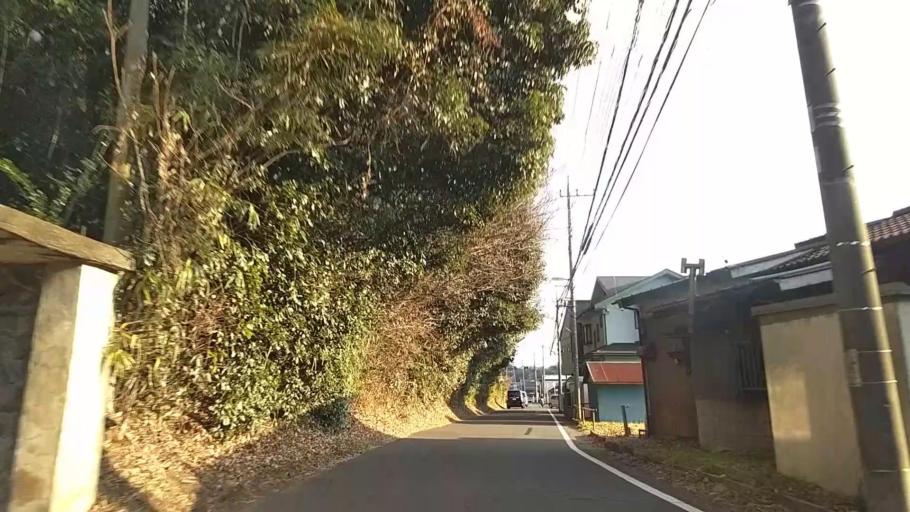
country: JP
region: Kanagawa
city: Atsugi
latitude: 35.4425
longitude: 139.3393
